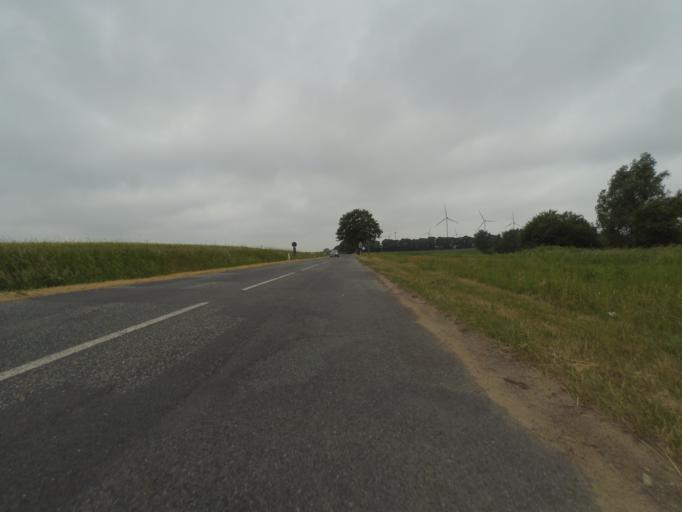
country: DE
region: Mecklenburg-Vorpommern
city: Plau am See
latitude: 53.4901
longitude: 12.2532
